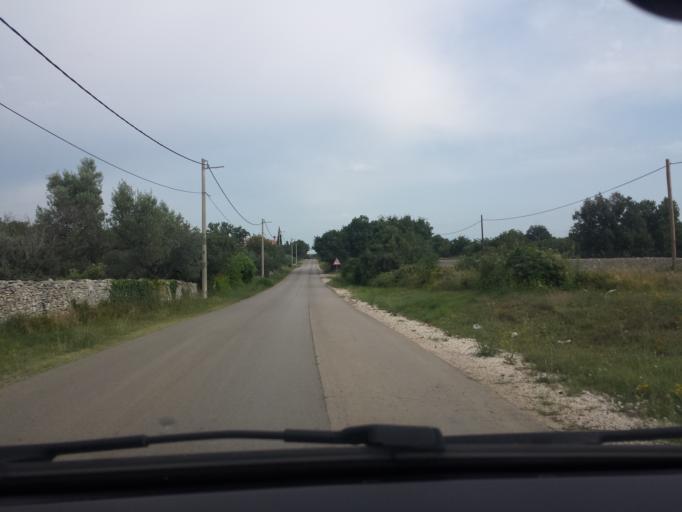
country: HR
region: Istarska
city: Galizana
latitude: 44.9382
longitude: 13.8686
